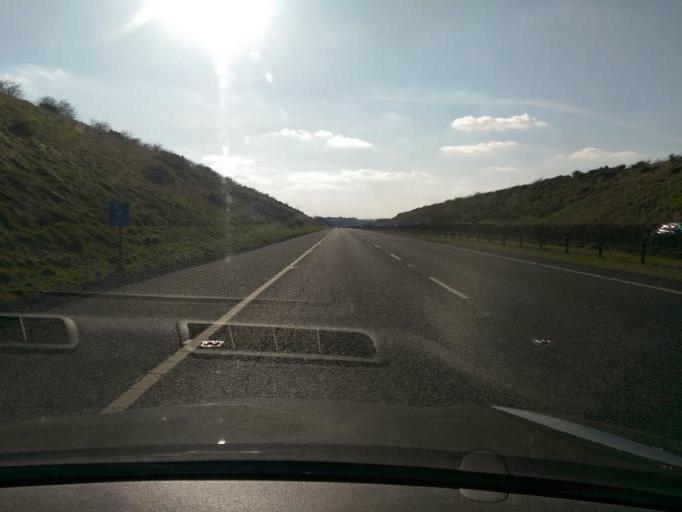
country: IE
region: Leinster
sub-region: Kildare
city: Kildare
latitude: 53.1553
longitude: -6.8722
